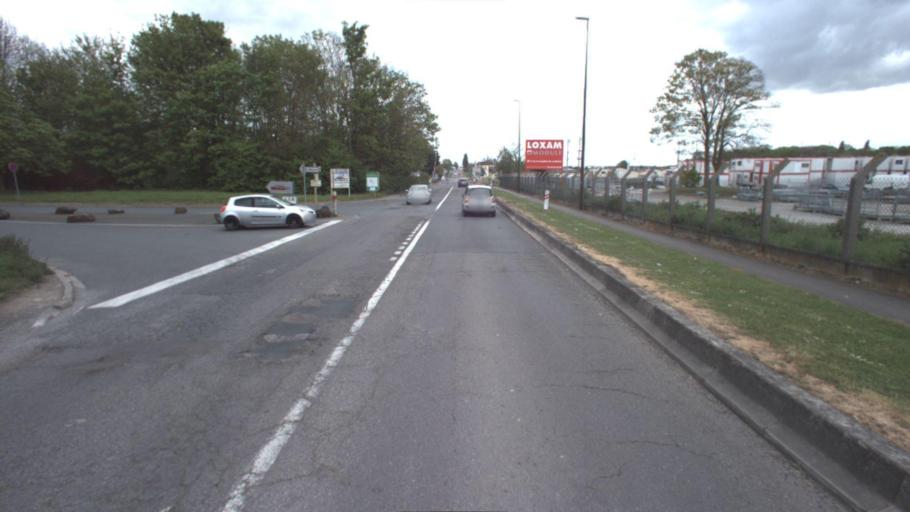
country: FR
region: Picardie
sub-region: Departement de l'Oise
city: Lagny-le-Sec
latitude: 49.0962
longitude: 2.7426
